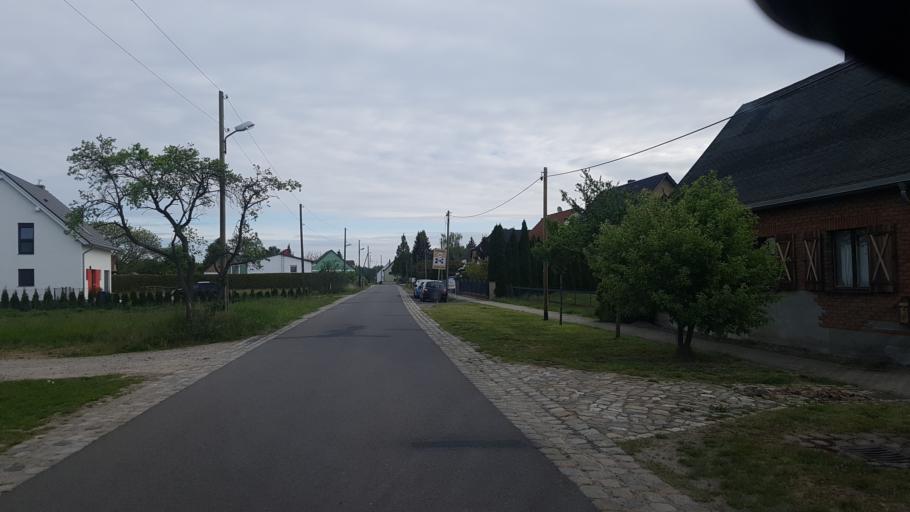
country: DE
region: Brandenburg
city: Luckenwalde
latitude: 52.1111
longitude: 13.1100
